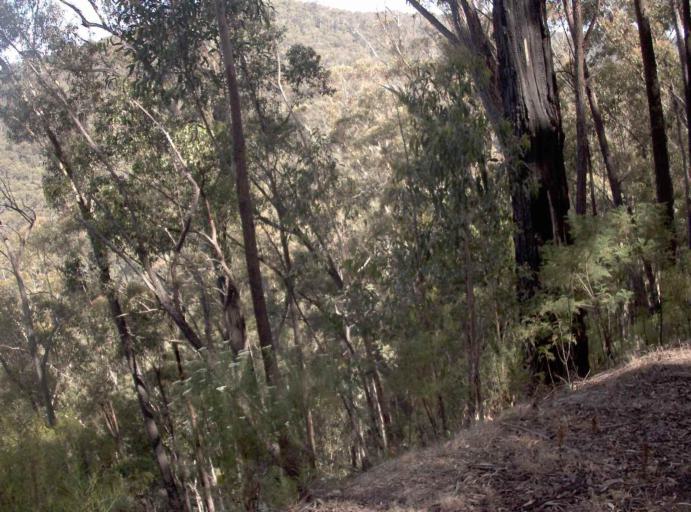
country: AU
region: Victoria
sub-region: East Gippsland
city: Lakes Entrance
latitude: -37.3970
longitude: 148.1225
